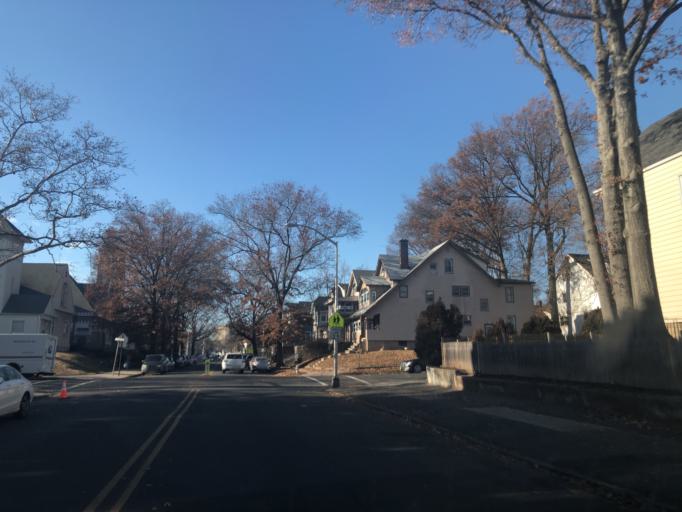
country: US
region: New Jersey
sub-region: Essex County
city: East Orange
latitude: 40.7535
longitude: -74.2185
